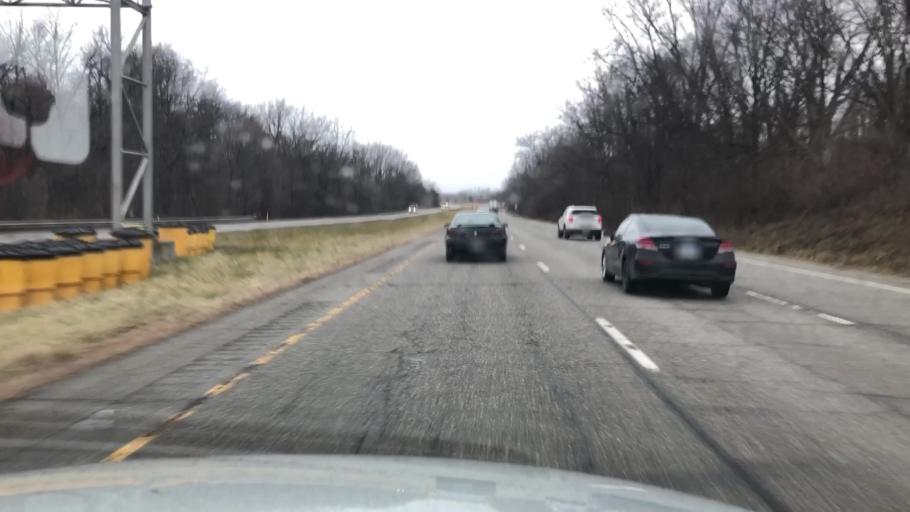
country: US
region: Indiana
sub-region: Marshall County
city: Plymouth
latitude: 41.3528
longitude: -86.2779
